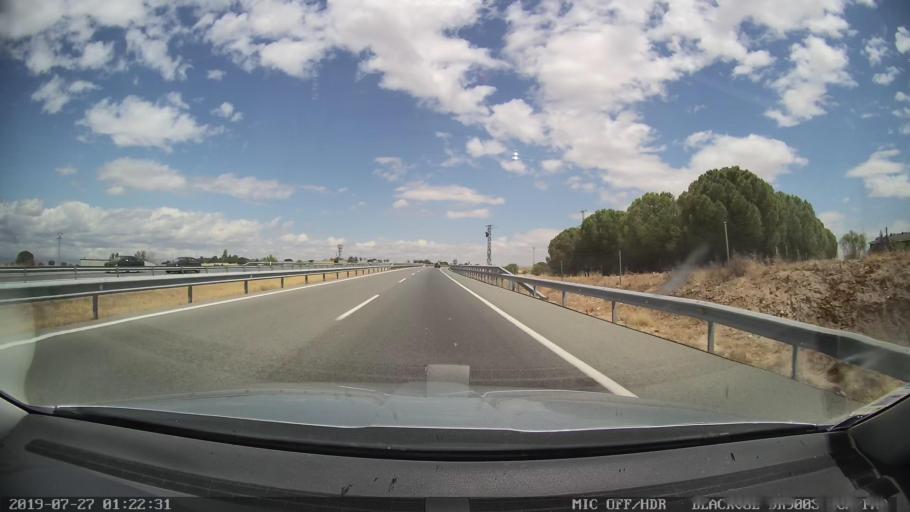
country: ES
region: Castille-La Mancha
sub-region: Province of Toledo
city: Santa Cruz del Retamar
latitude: 40.1231
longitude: -4.2551
